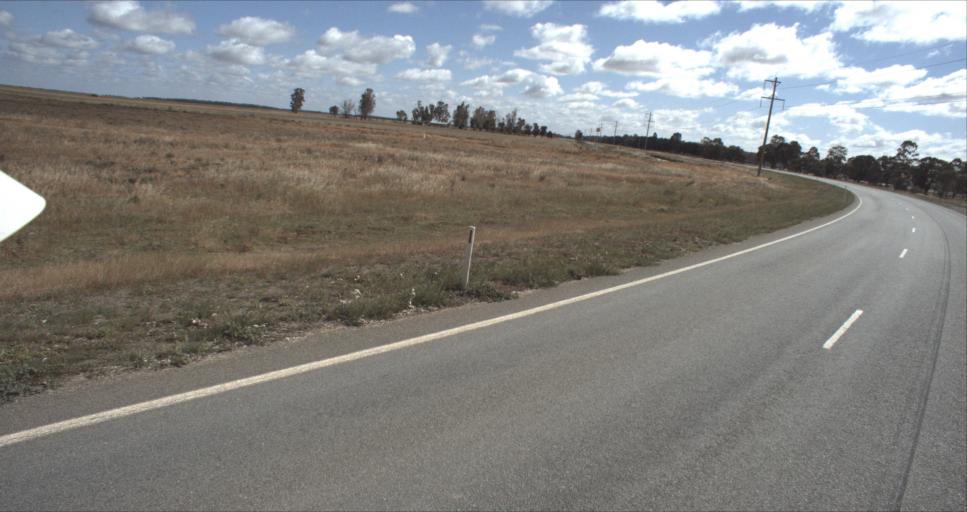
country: AU
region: New South Wales
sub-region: Murrumbidgee Shire
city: Darlington Point
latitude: -34.5969
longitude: 146.1616
